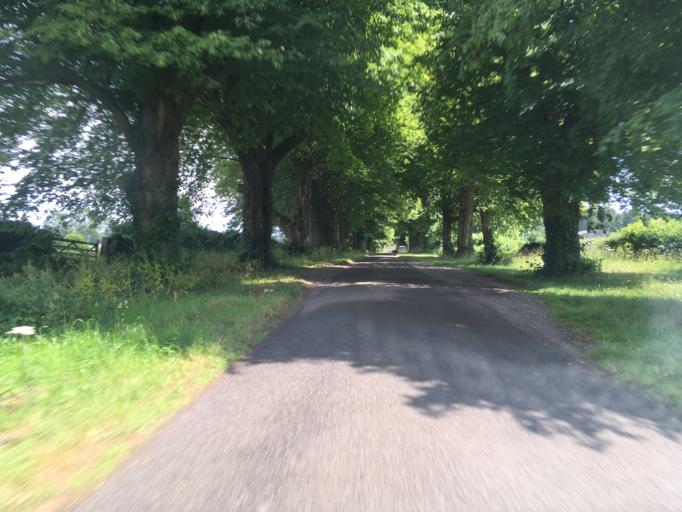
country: GB
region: England
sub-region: Gloucestershire
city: Tetbury
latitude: 51.6580
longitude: -2.1899
